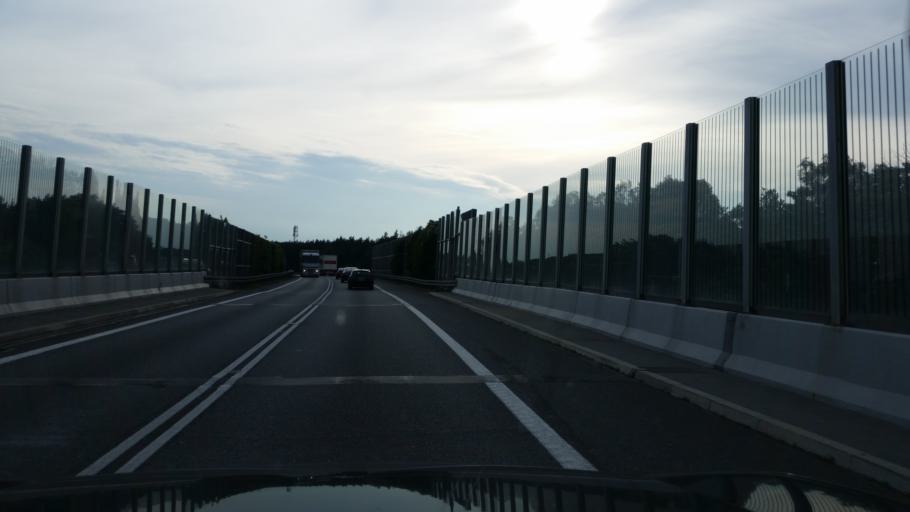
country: PL
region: Silesian Voivodeship
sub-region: Powiat bedzinski
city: Mierzecice
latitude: 50.4571
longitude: 19.0958
